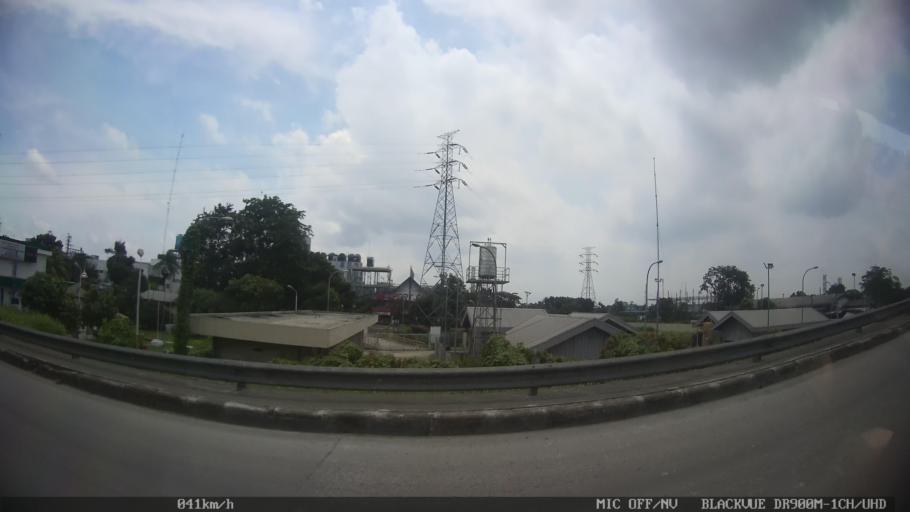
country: ID
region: North Sumatra
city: Labuhan Deli
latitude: 3.6731
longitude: 98.6819
